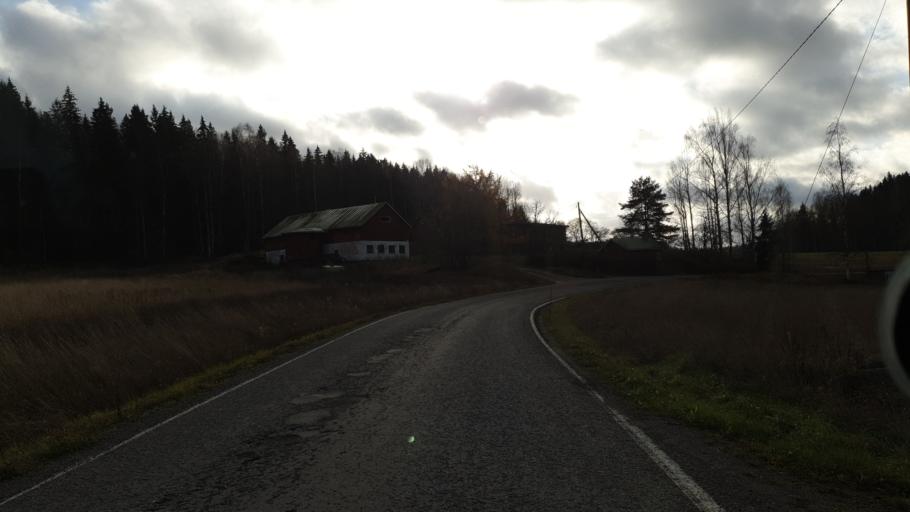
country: FI
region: Uusimaa
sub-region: Helsinki
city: Siuntio
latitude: 60.2541
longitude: 24.2994
